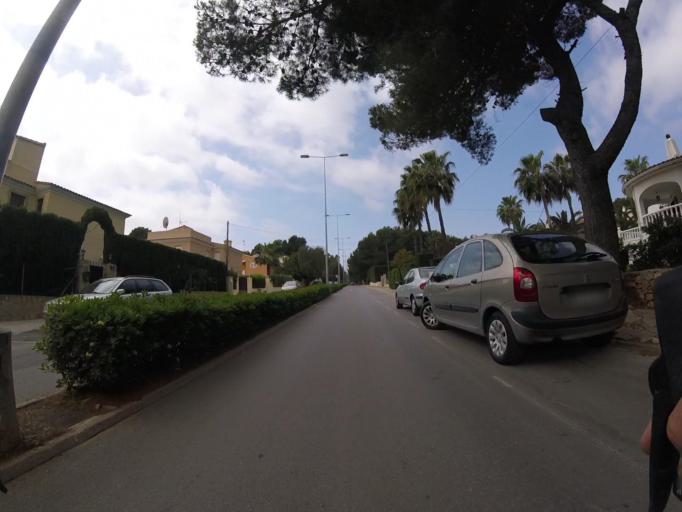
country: ES
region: Valencia
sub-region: Provincia de Castello
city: Alcoceber
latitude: 40.2554
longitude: 0.2863
